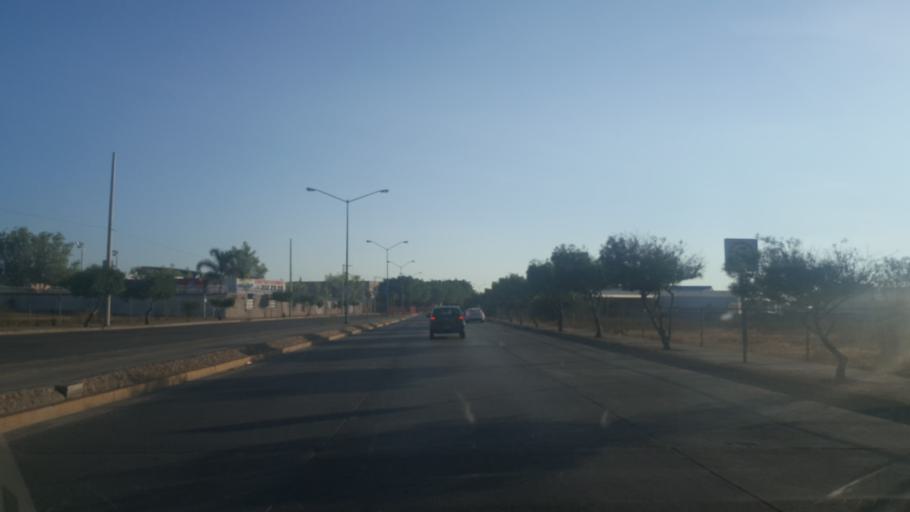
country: MX
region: Guanajuato
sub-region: Leon
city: Medina
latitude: 21.1236
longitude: -101.6306
